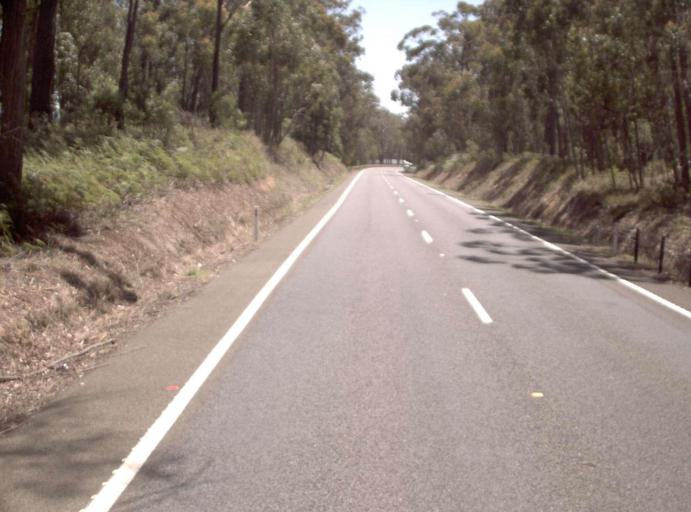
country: AU
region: Victoria
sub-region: East Gippsland
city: Lakes Entrance
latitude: -37.7819
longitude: 148.0526
